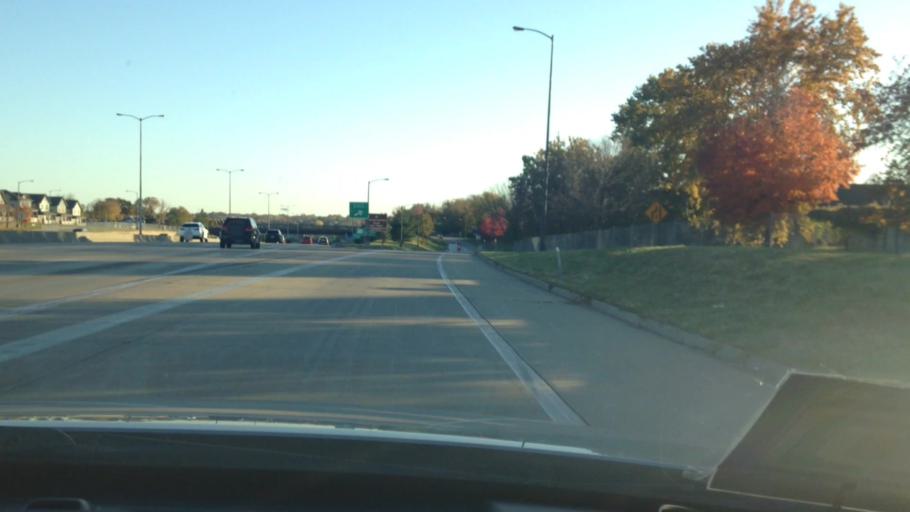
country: US
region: Missouri
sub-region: Jackson County
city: Kansas City
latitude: 39.0595
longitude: -94.5612
